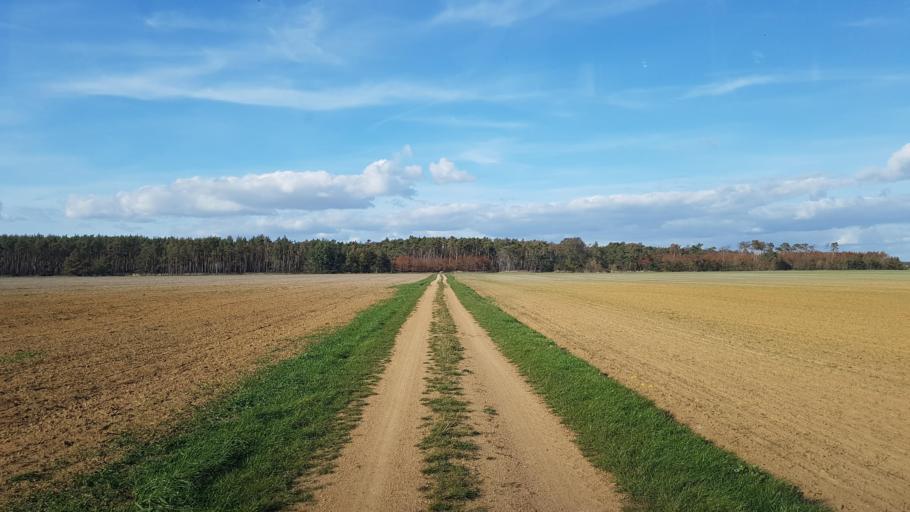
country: DE
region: Brandenburg
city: Muhlberg
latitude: 51.4480
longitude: 13.3100
